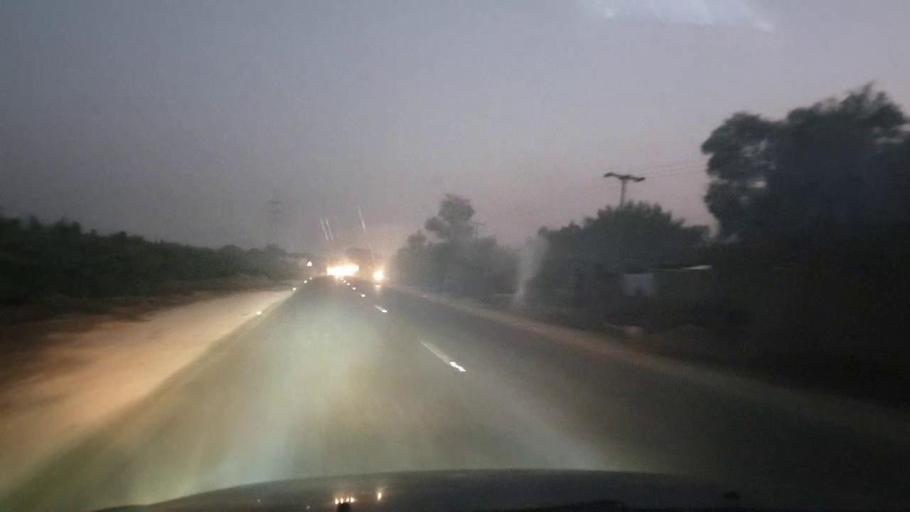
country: PK
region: Sindh
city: Chambar
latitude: 25.3663
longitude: 68.7837
